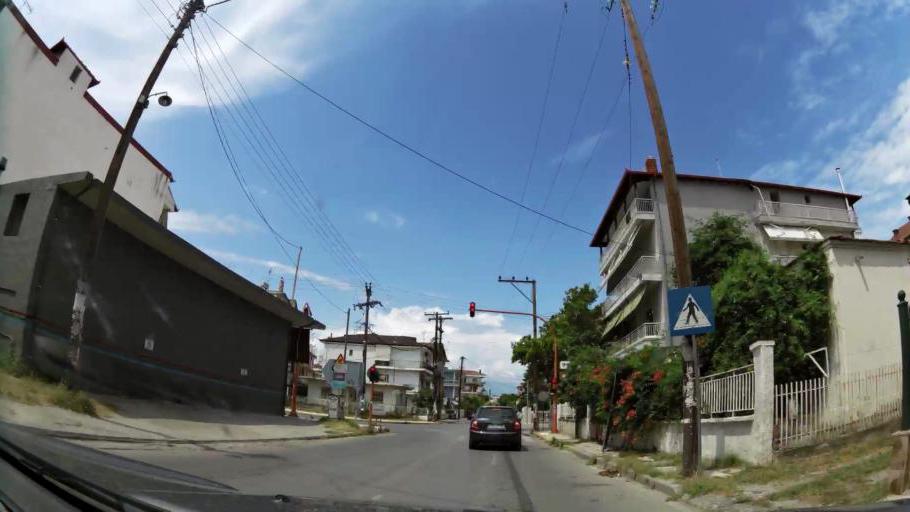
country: GR
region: Central Macedonia
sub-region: Nomos Pierias
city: Katerini
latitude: 40.2668
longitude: 22.5085
